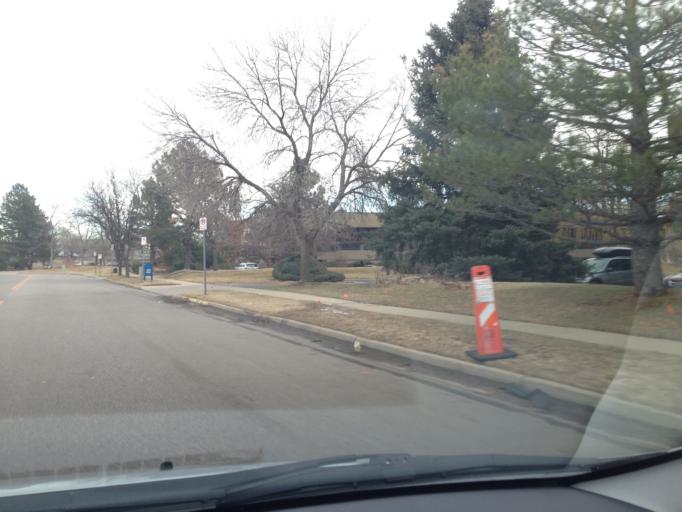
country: US
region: Colorado
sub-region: Boulder County
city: Boulder
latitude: 40.0158
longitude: -105.2450
